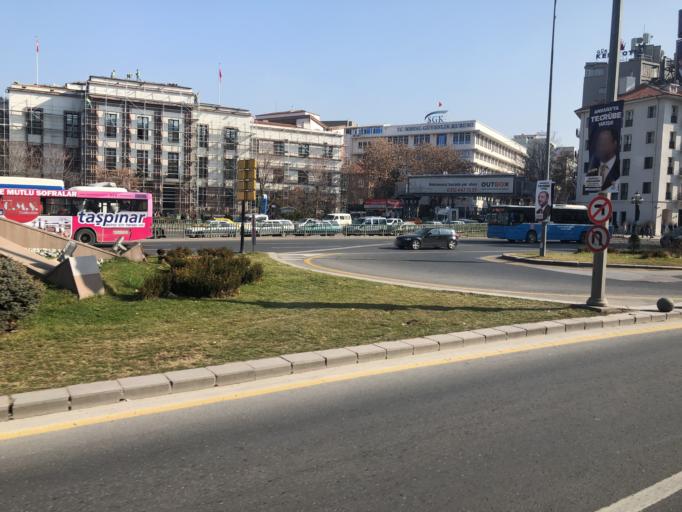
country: TR
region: Ankara
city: Ankara
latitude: 39.9270
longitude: 32.8549
